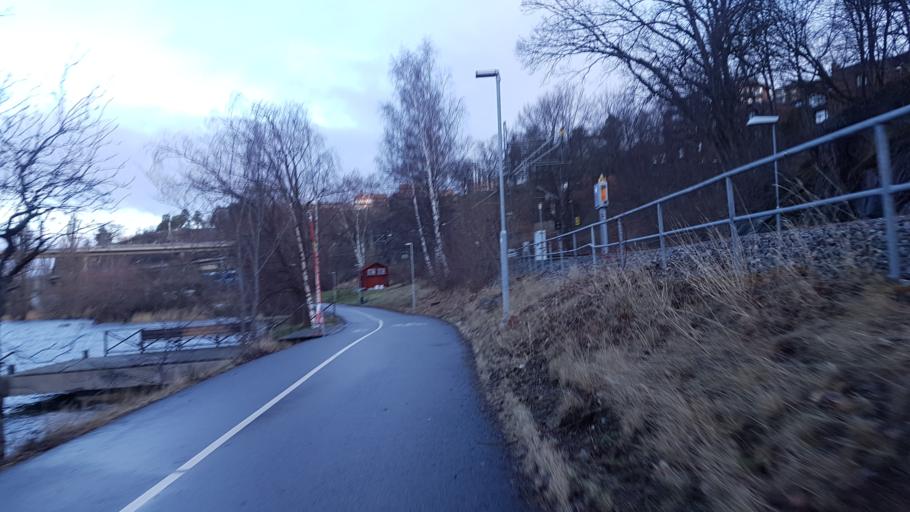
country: SE
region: Stockholm
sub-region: Lidingo
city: Lidingoe
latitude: 59.3604
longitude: 18.1178
